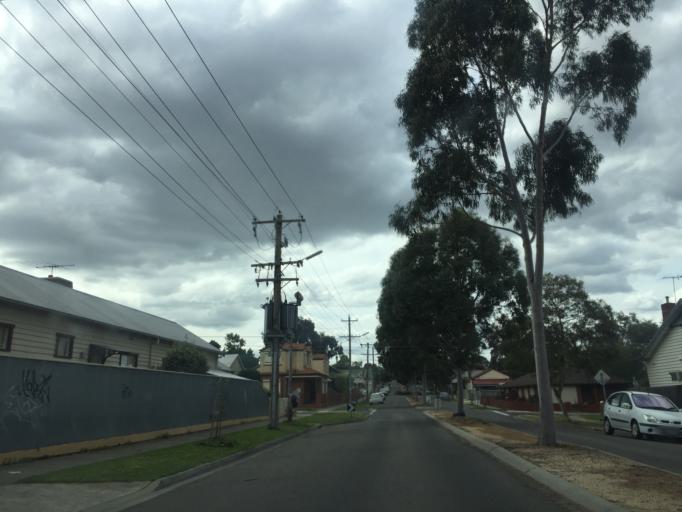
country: AU
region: Victoria
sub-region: Darebin
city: Thornbury
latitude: -37.7602
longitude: 145.0094
